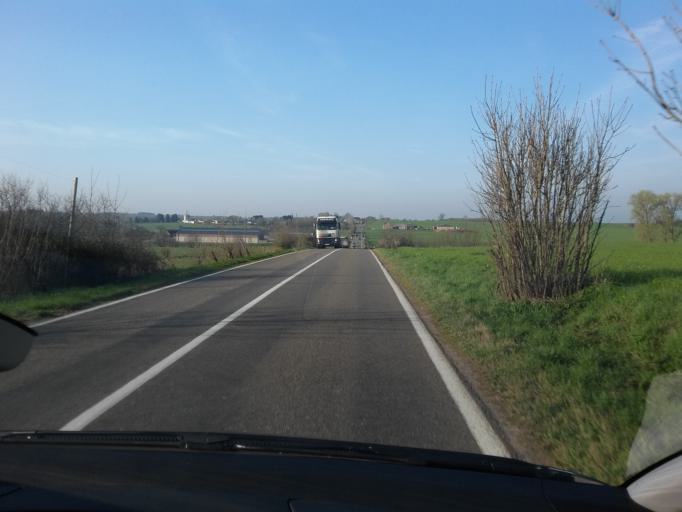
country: BE
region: Wallonia
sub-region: Province du Luxembourg
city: Etalle
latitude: 49.6887
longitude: 5.6106
